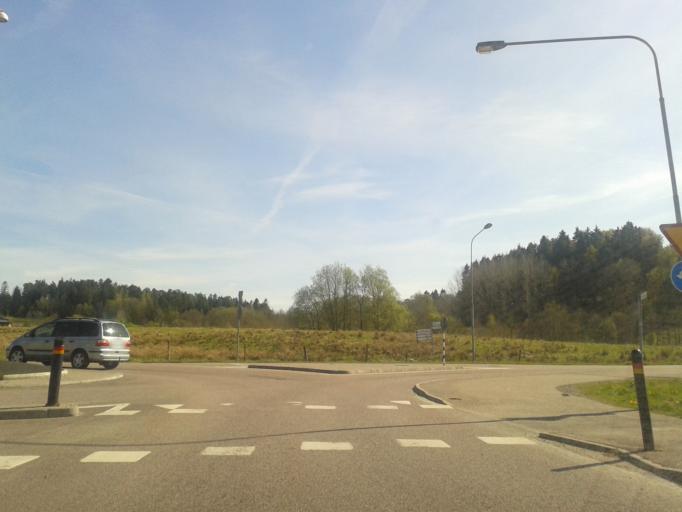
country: SE
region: Vaestra Goetaland
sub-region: Ale Kommun
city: Nodinge-Nol
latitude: 57.8911
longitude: 12.0678
